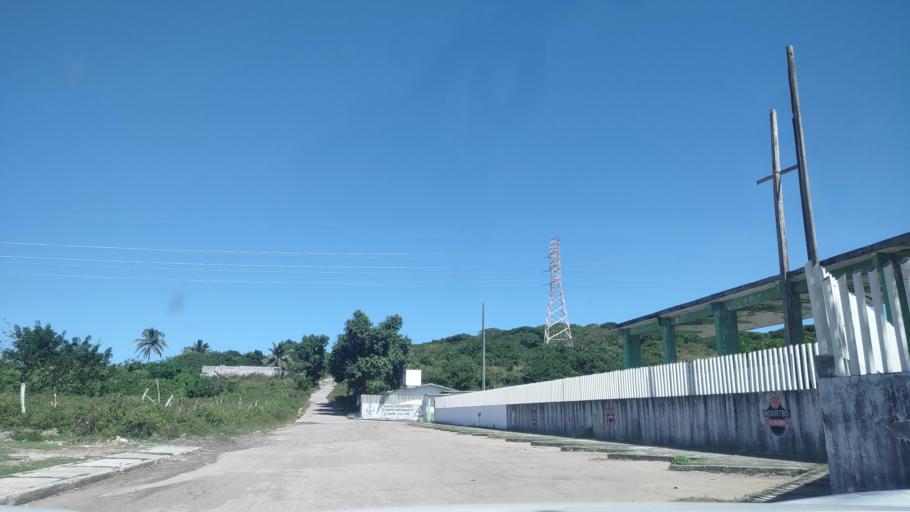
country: MX
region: Veracruz
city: Heroica Alvarado
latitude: 18.7832
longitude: -95.7698
